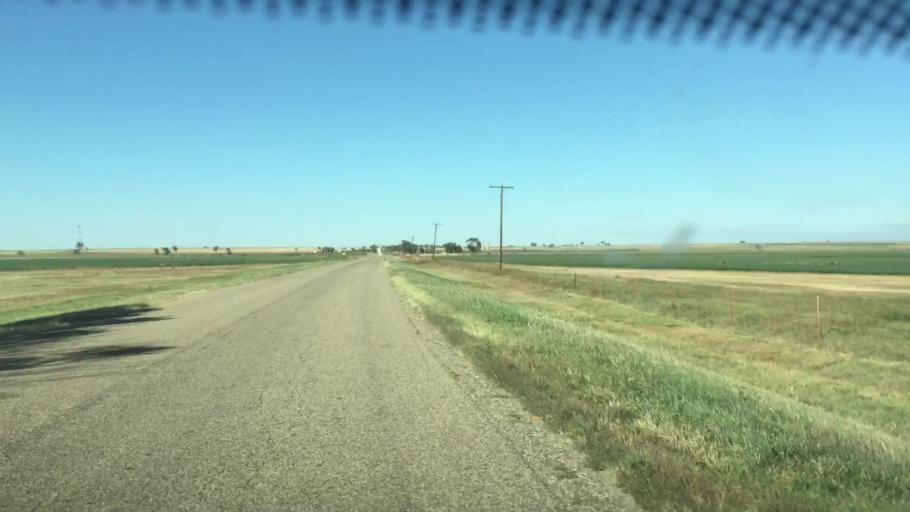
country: US
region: Colorado
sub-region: Prowers County
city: Lamar
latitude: 38.1015
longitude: -102.5215
